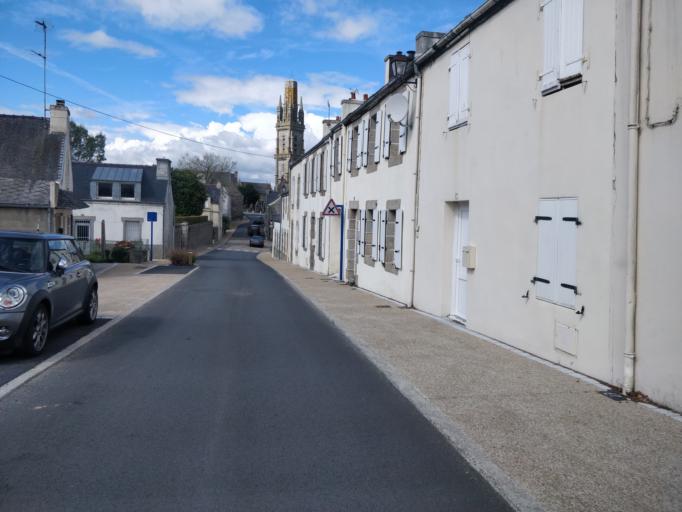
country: FR
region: Brittany
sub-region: Departement du Finistere
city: Lampaul-Guimiliau
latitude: 48.4925
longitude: -4.0381
